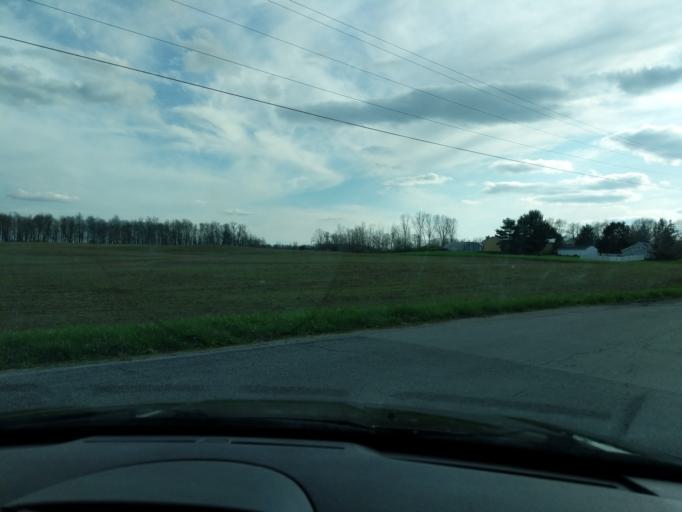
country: US
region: Ohio
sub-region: Champaign County
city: Urbana
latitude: 40.1382
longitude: -83.7160
